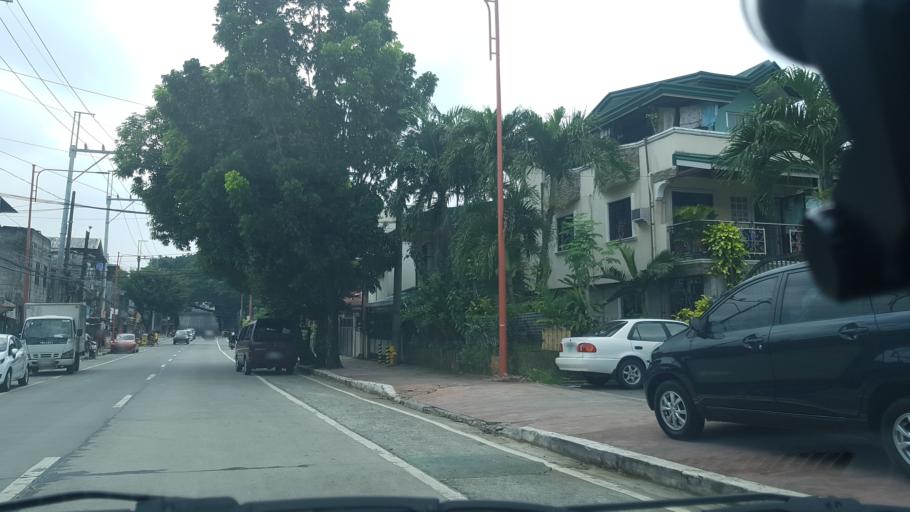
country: PH
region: Calabarzon
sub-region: Province of Rizal
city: Antipolo
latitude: 14.6494
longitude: 121.1214
